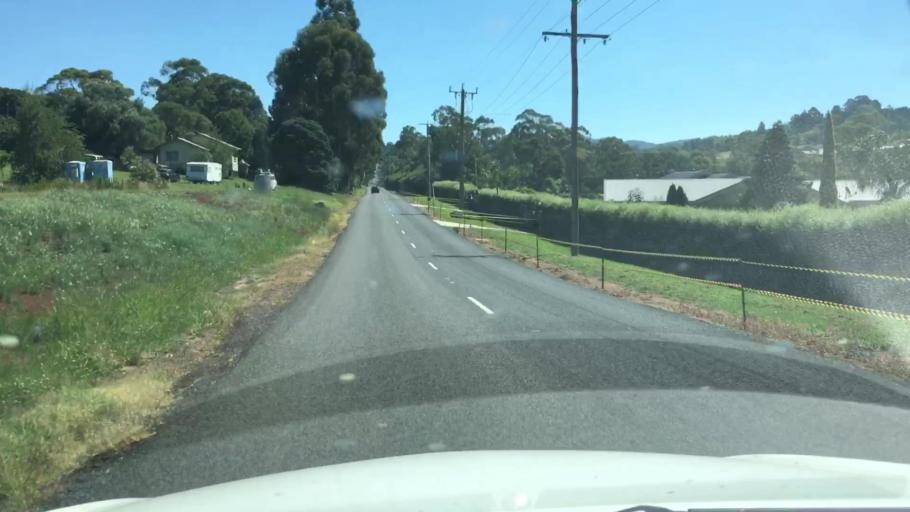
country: AU
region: Victoria
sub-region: Yarra Ranges
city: Mount Evelyn
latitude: -37.7993
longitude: 145.4488
